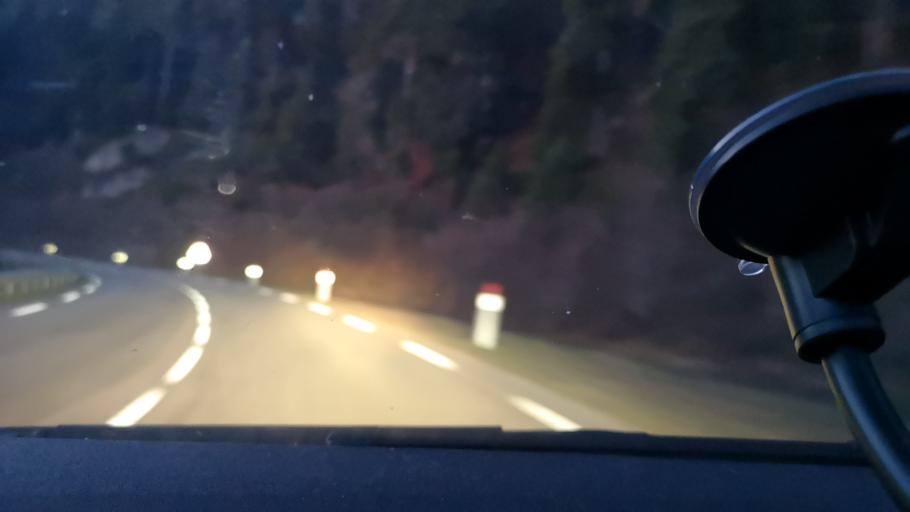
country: FR
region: Franche-Comte
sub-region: Departement du Jura
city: Champagnole
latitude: 46.7574
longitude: 5.9671
